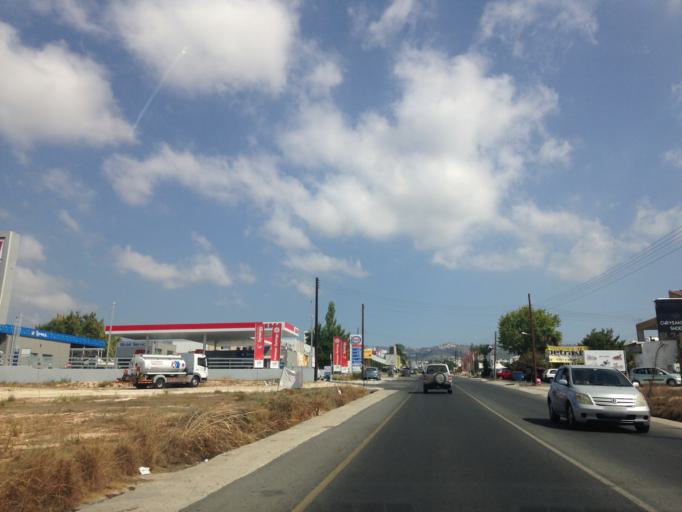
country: CY
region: Pafos
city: Empa
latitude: 34.7988
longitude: 32.4409
